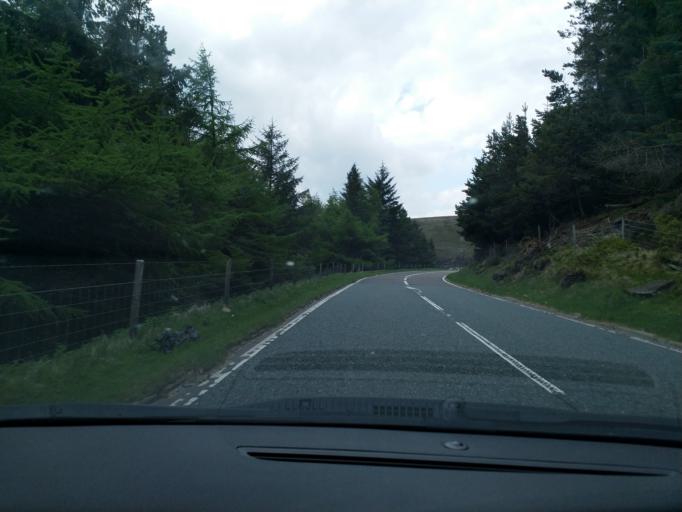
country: GB
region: England
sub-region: Derbyshire
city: High Peak
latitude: 53.4286
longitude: -1.8456
